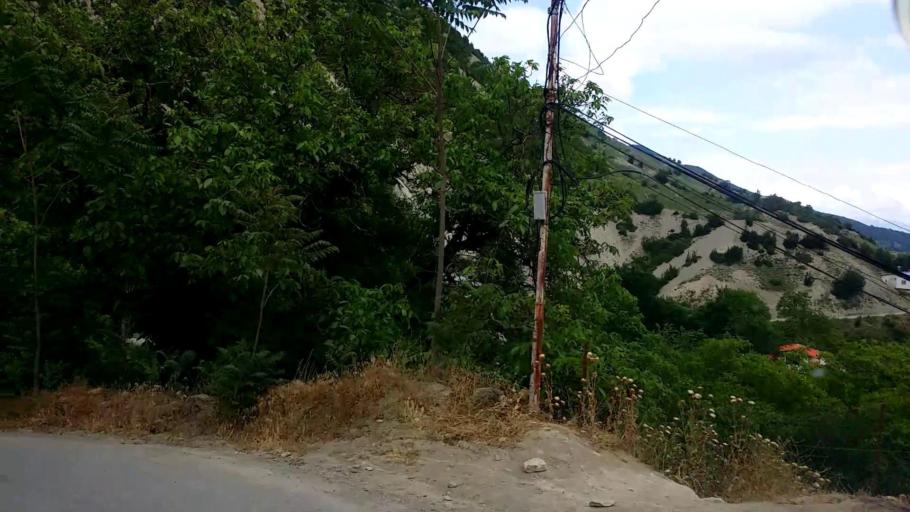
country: IR
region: Mazandaran
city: Chalus
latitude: 36.5554
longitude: 51.2741
